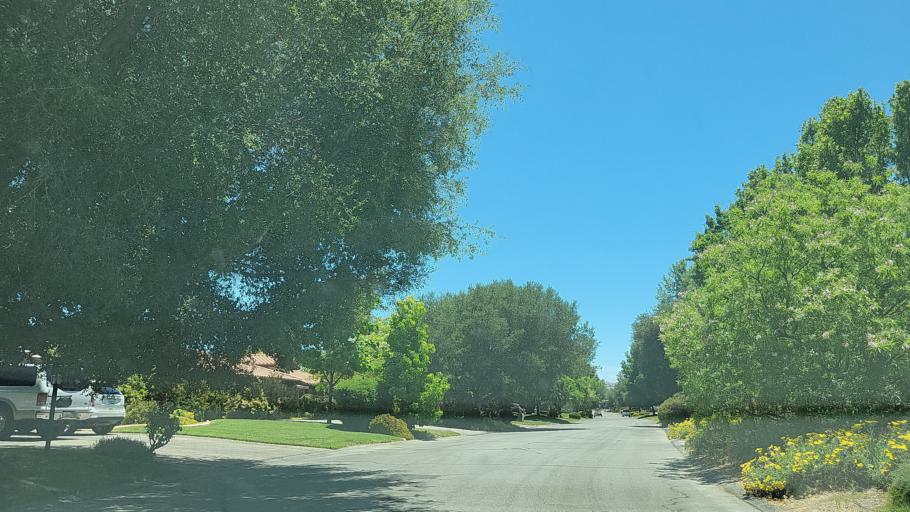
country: US
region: California
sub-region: San Luis Obispo County
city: Atascadero
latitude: 35.5175
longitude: -120.6755
